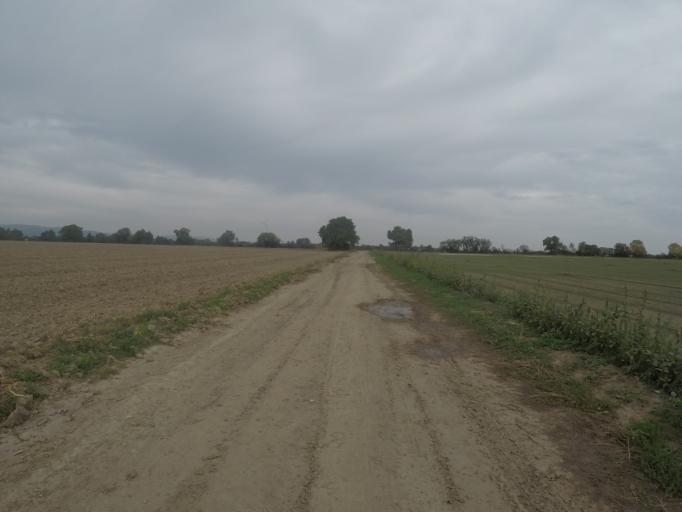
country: DE
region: Rheinland-Pfalz
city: Hassloch
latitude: 49.3684
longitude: 8.2811
